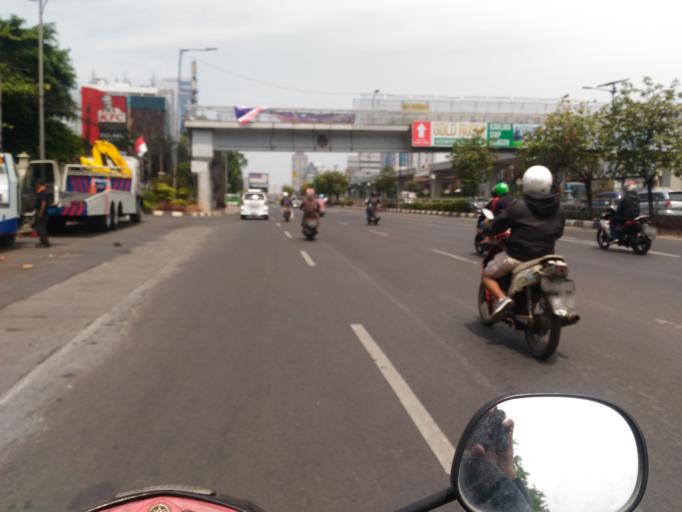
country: ID
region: Jakarta Raya
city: Jakarta
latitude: -6.2431
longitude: 106.8467
